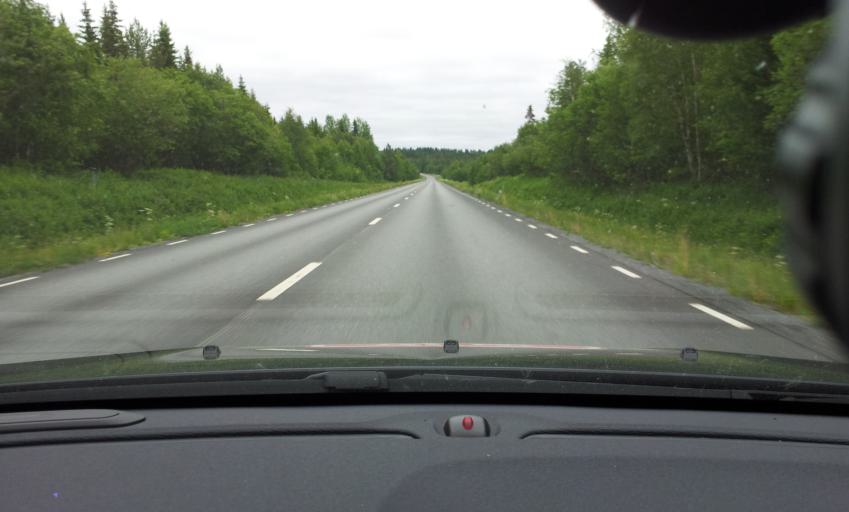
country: SE
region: Jaemtland
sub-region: Krokoms Kommun
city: Krokom
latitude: 63.0866
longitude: 14.2965
